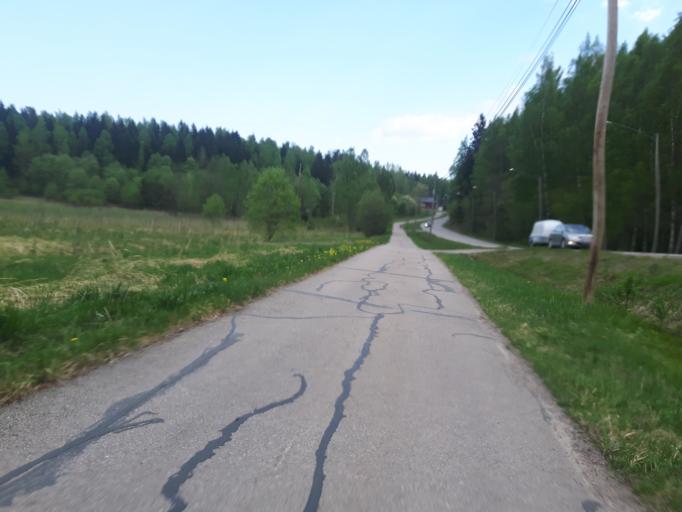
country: FI
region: Uusimaa
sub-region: Porvoo
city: Porvoo
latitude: 60.4000
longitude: 25.7275
